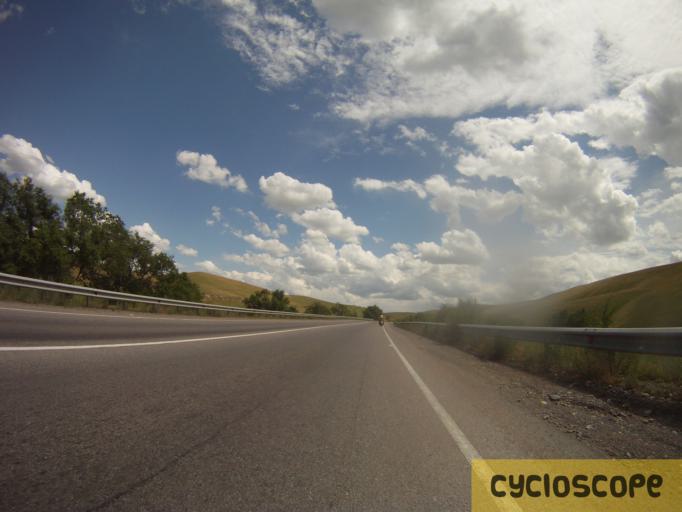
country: KZ
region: Almaty Oblysy
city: Burunday
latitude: 43.2945
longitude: 76.2338
